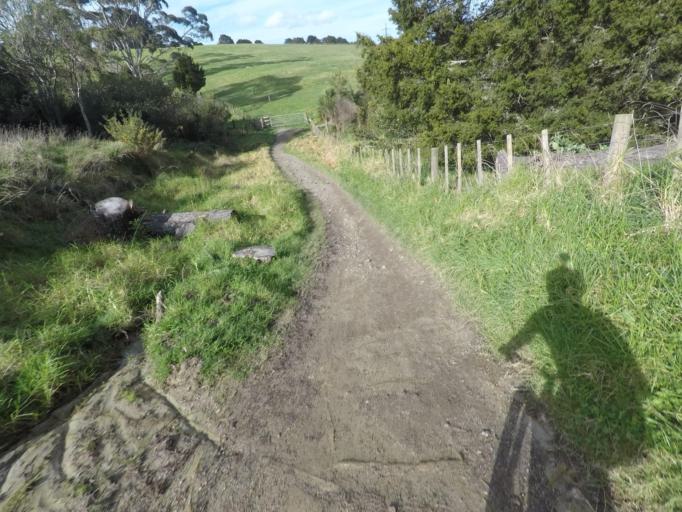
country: NZ
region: Auckland
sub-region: Auckland
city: Manukau City
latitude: -36.9927
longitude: 174.9118
